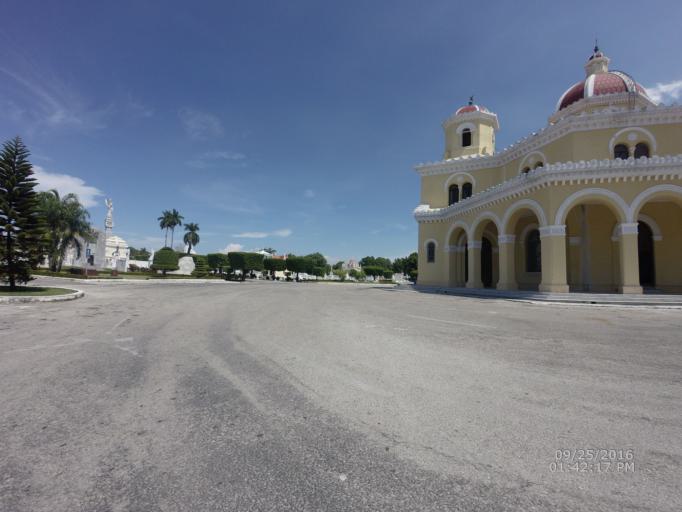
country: CU
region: La Habana
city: Havana
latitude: 23.1232
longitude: -82.3992
